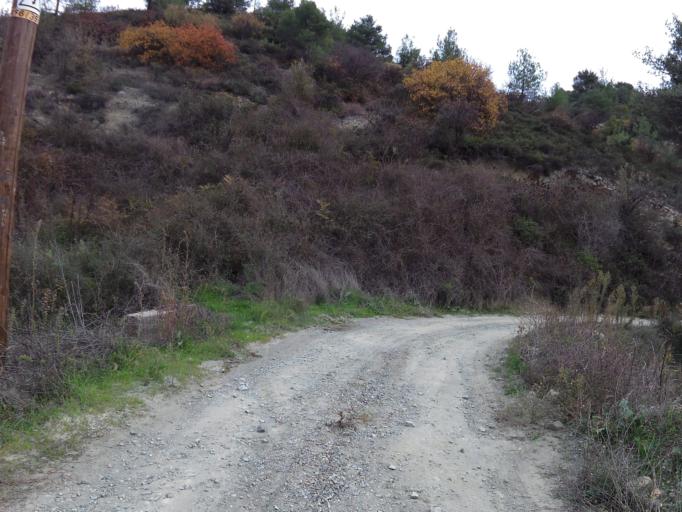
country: CY
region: Limassol
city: Kyperounta
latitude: 34.9229
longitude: 32.9464
